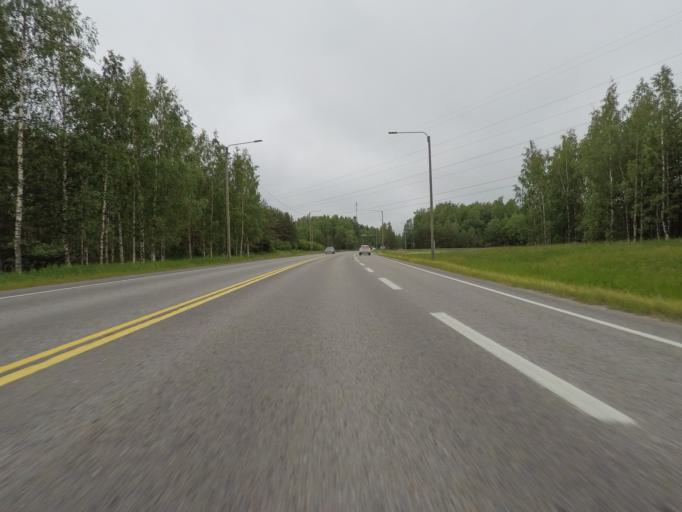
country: FI
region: Varsinais-Suomi
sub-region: Turku
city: Raisio
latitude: 60.4643
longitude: 22.1054
